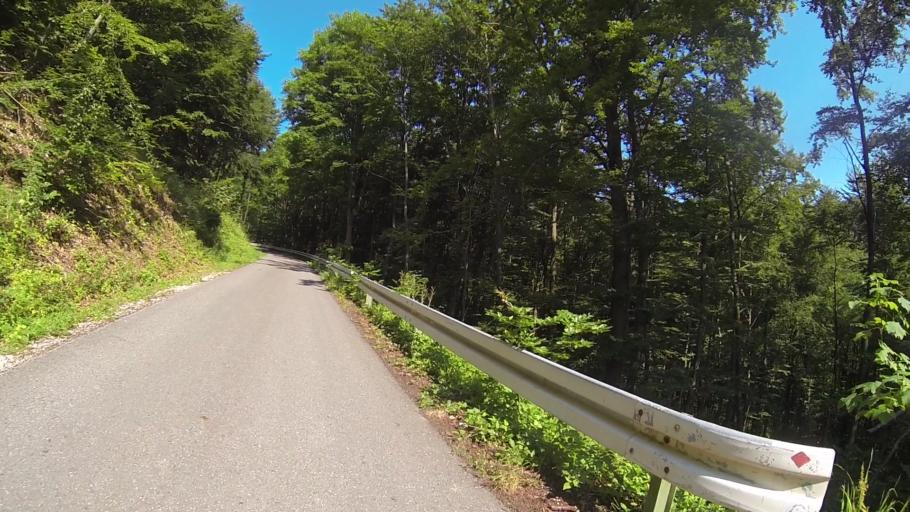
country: DE
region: Baden-Wuerttemberg
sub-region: Regierungsbezirk Stuttgart
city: Oberkochen
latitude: 48.7845
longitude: 10.0893
